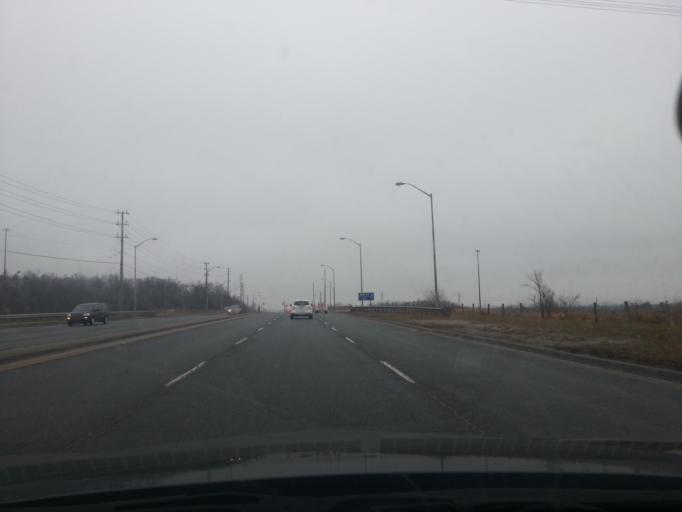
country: CA
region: Ontario
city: Concord
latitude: 43.8263
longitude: -79.4536
